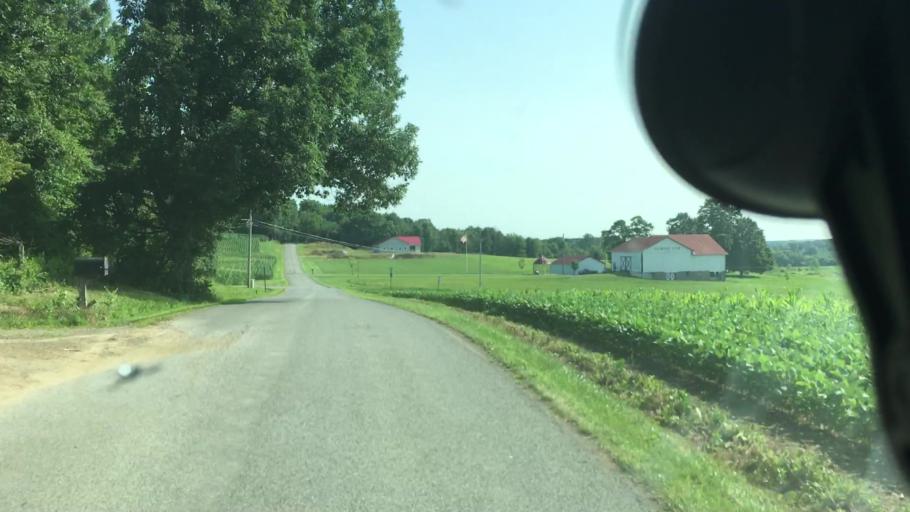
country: US
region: Pennsylvania
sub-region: Butler County
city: Slippery Rock
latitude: 41.0497
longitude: -80.1746
